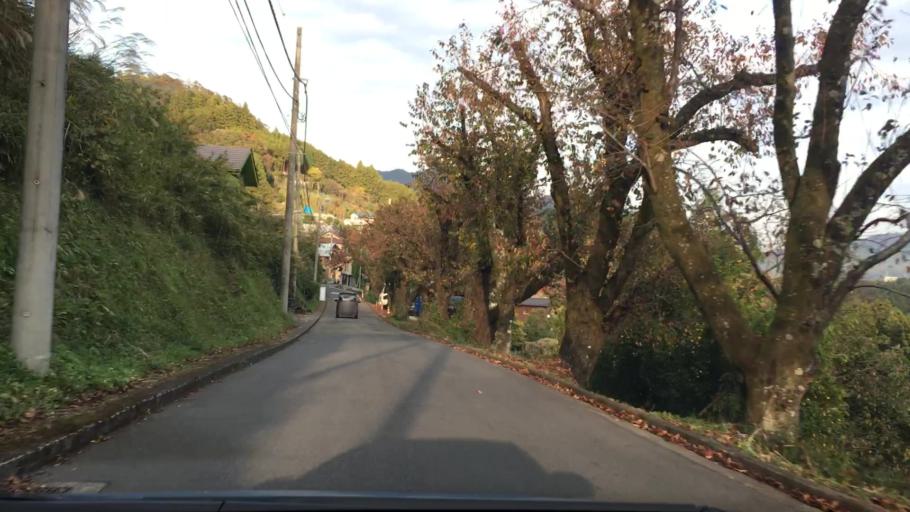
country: JP
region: Yamanashi
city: Uenohara
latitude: 35.5585
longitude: 139.1632
